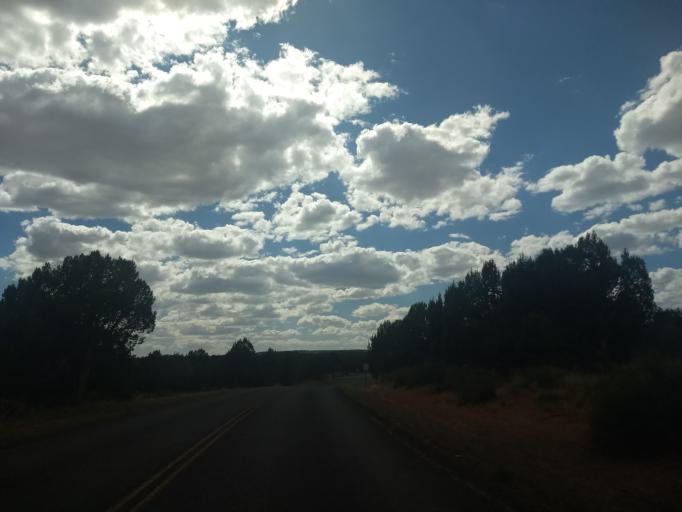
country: US
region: Utah
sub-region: Kane County
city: Kanab
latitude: 37.1455
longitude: -112.5552
